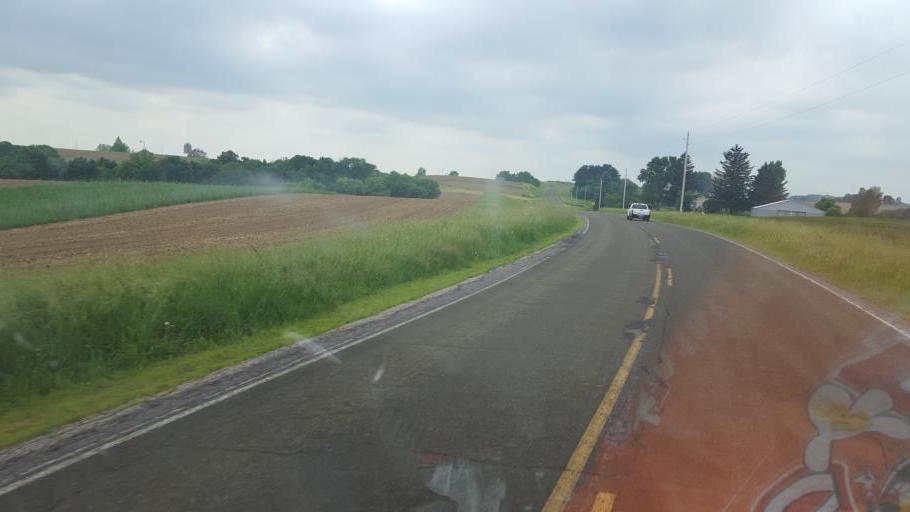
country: US
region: Wisconsin
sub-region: Juneau County
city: Elroy
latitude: 43.6518
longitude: -90.2514
